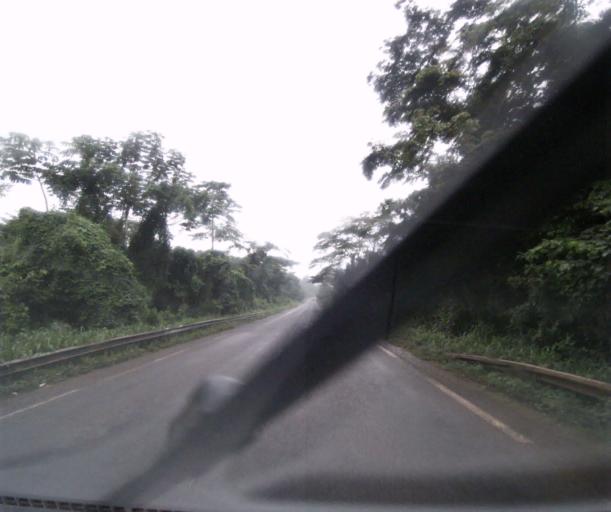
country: CM
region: Centre
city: Eseka
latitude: 3.8903
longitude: 10.7580
